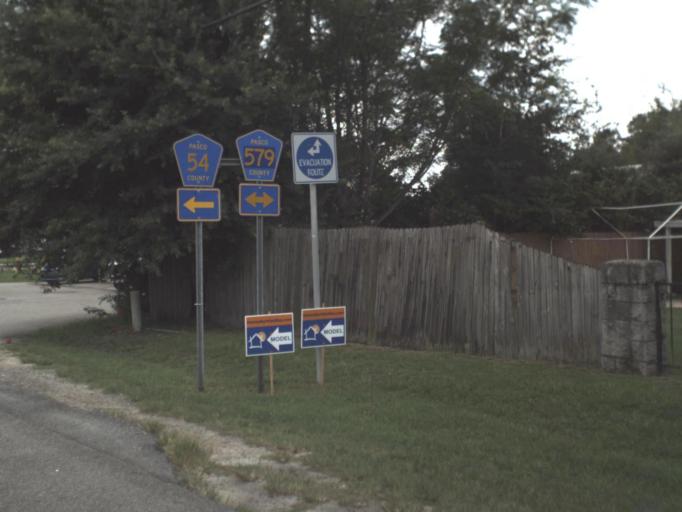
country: US
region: Florida
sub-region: Pasco County
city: Zephyrhills West
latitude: 28.2188
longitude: -82.2468
